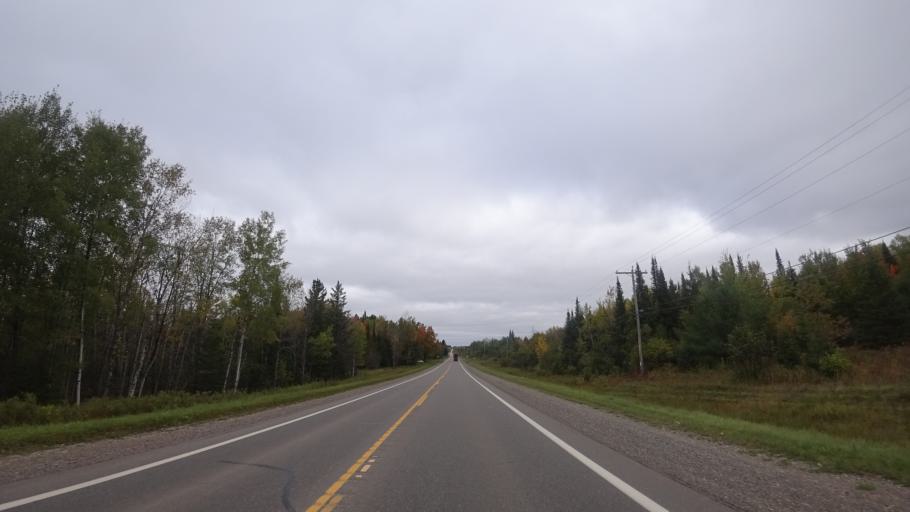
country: US
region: Wisconsin
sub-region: Florence County
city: Florence
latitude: 46.0950
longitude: -88.0758
